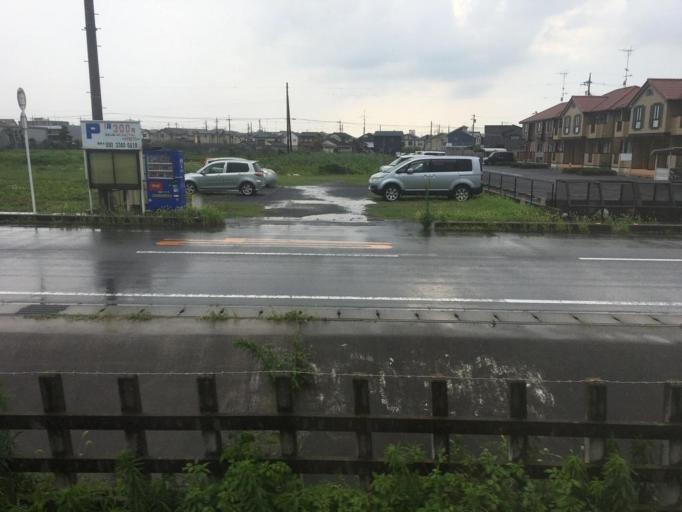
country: JP
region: Tochigi
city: Ashikaga
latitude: 36.3168
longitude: 139.4549
